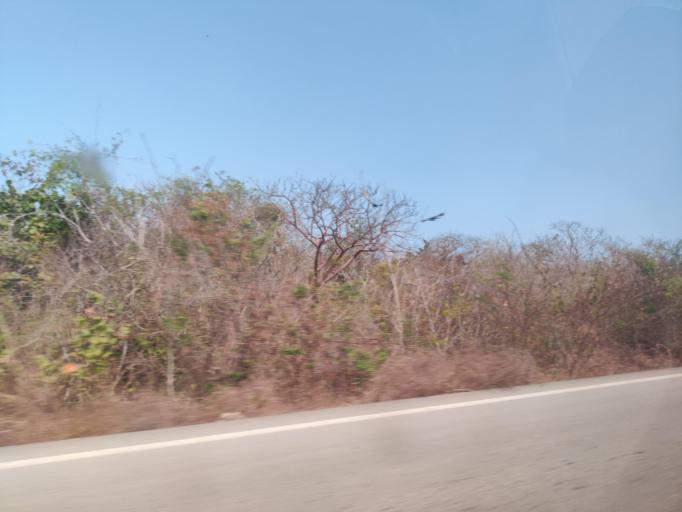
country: CO
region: Bolivar
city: Turbana
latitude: 10.1804
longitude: -75.6452
